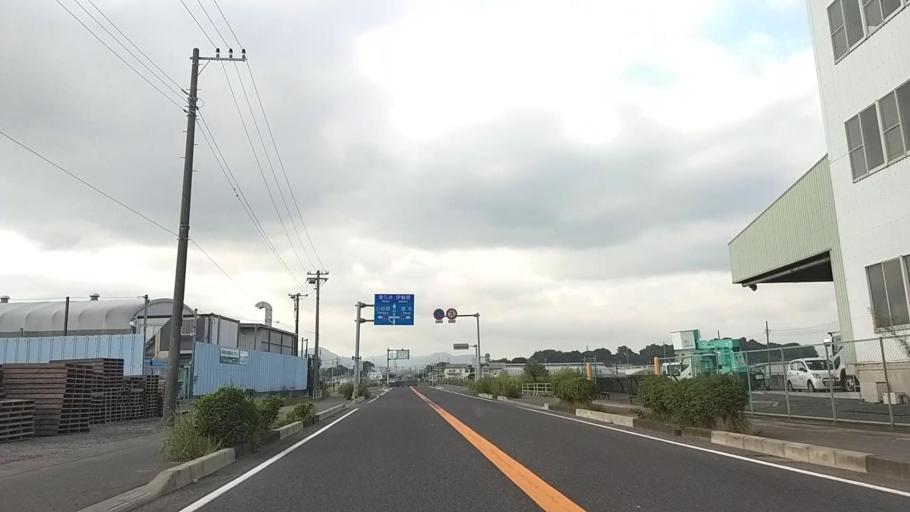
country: JP
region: Kanagawa
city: Isehara
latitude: 35.3715
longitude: 139.3211
